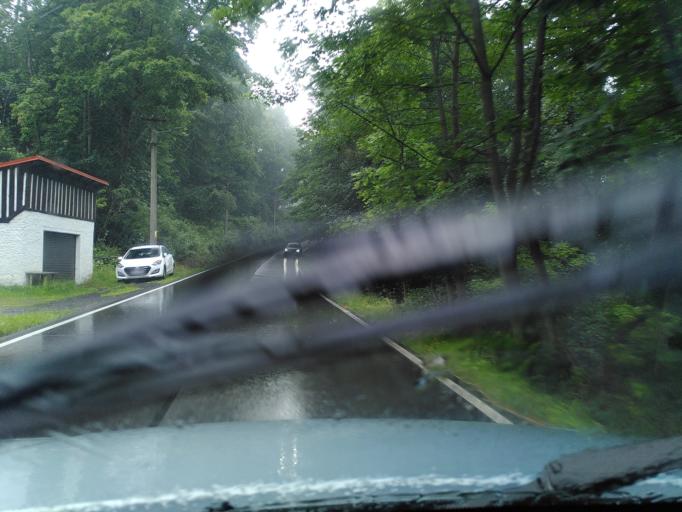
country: CZ
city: Novy Bor
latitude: 50.8084
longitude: 14.5395
